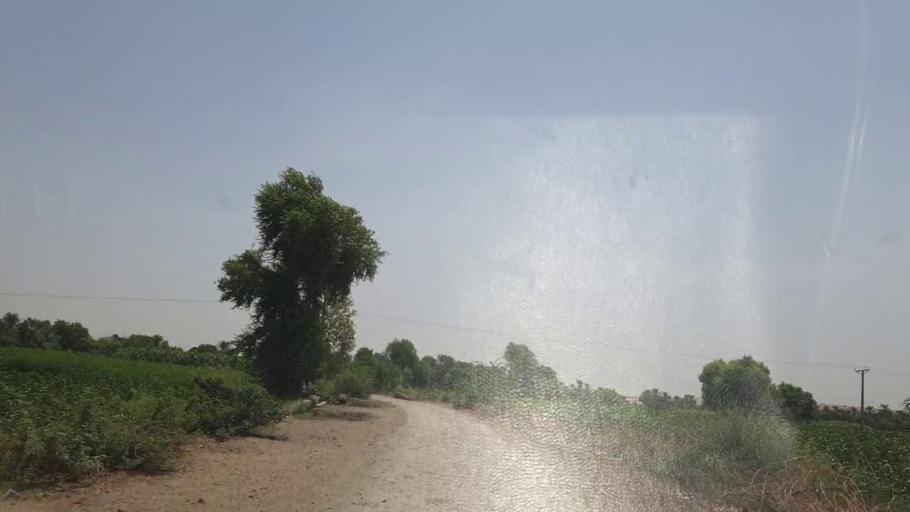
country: PK
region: Sindh
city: Bozdar
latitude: 27.2491
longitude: 68.6827
